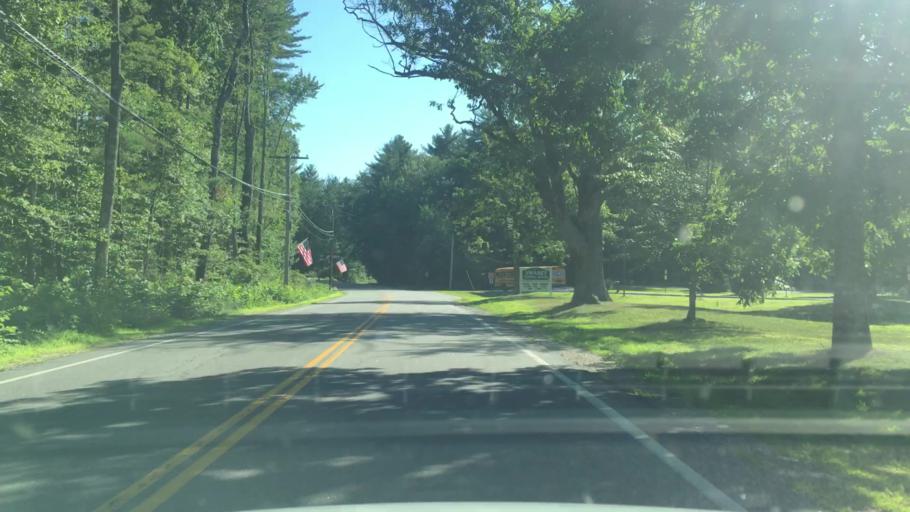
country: US
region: New Hampshire
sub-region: Rockingham County
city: Brentwood
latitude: 42.9840
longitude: -71.0656
